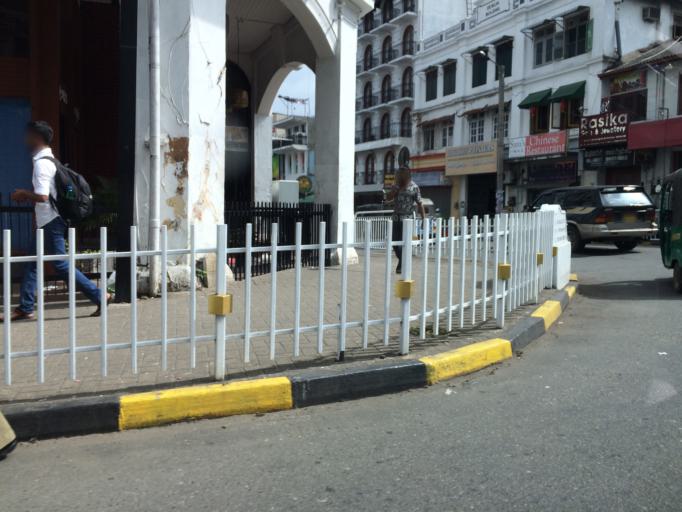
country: LK
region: Central
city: Kandy
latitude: 7.2931
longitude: 80.6370
